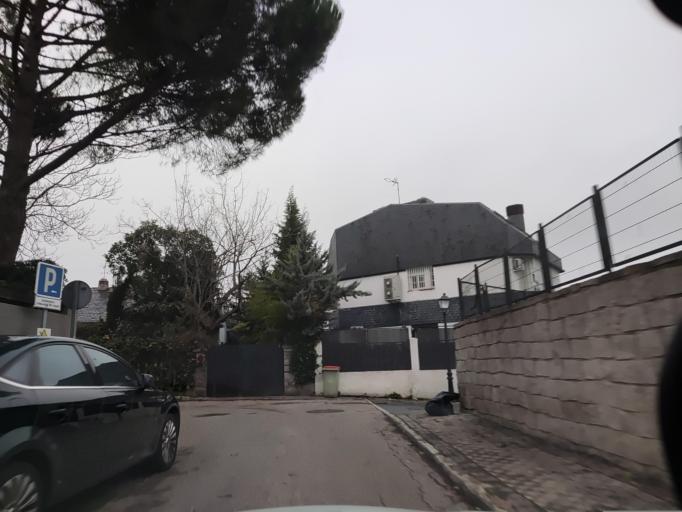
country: ES
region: Madrid
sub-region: Provincia de Madrid
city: Tetuan de las Victorias
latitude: 40.4900
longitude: -3.7007
